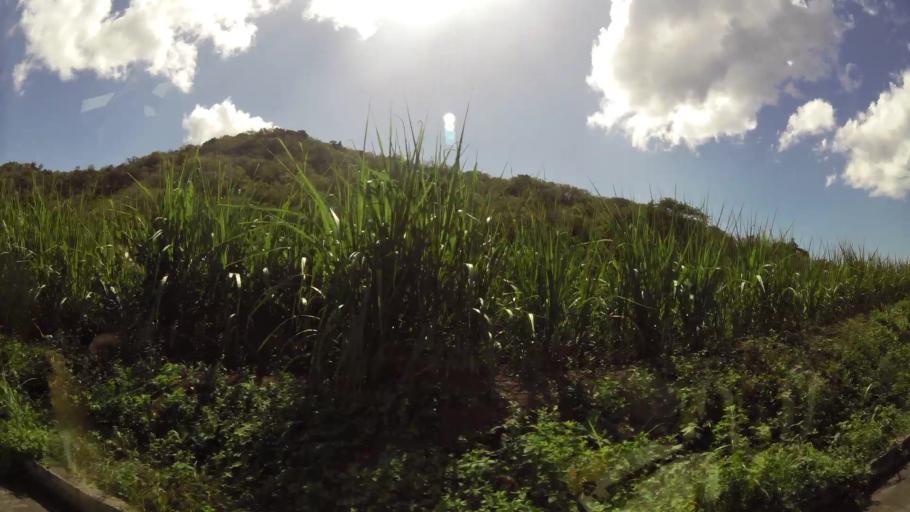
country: MQ
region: Martinique
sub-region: Martinique
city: Saint-Pierre
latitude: 14.6993
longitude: -61.1761
